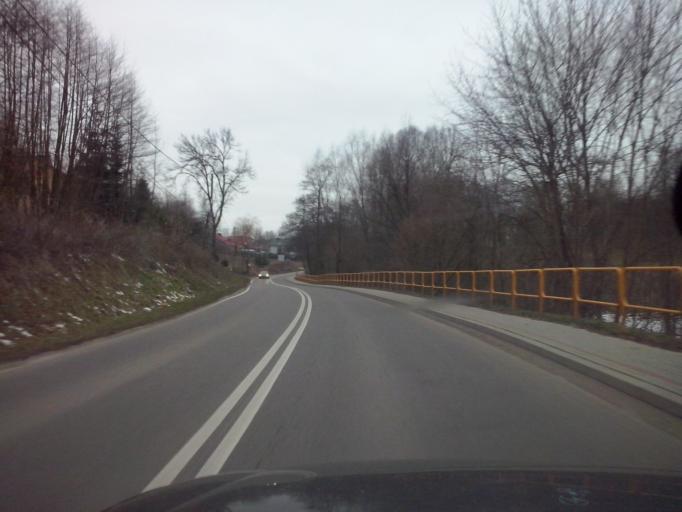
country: PL
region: Subcarpathian Voivodeship
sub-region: Powiat nizanski
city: Krzeszow
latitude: 50.4082
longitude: 22.3432
